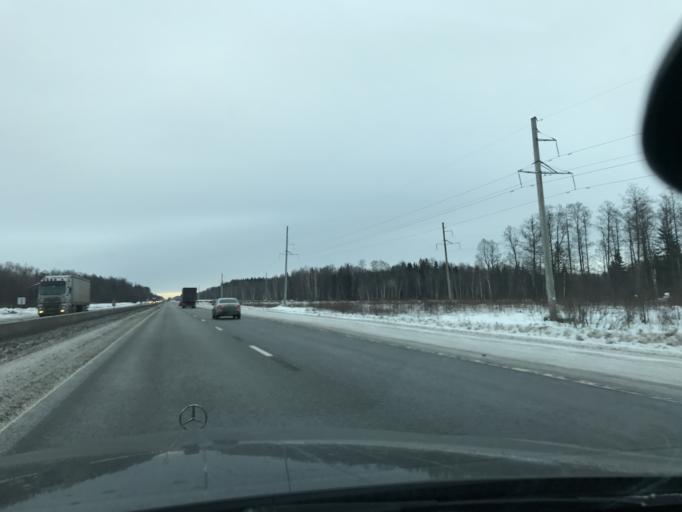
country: RU
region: Nizjnij Novgorod
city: Smolino
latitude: 56.2831
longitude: 43.1230
